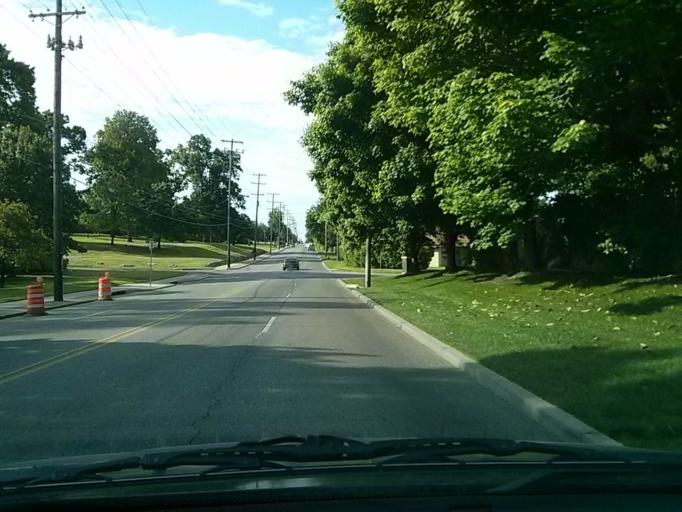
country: US
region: Oklahoma
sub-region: Tulsa County
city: Tulsa
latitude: 36.1321
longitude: -95.9757
